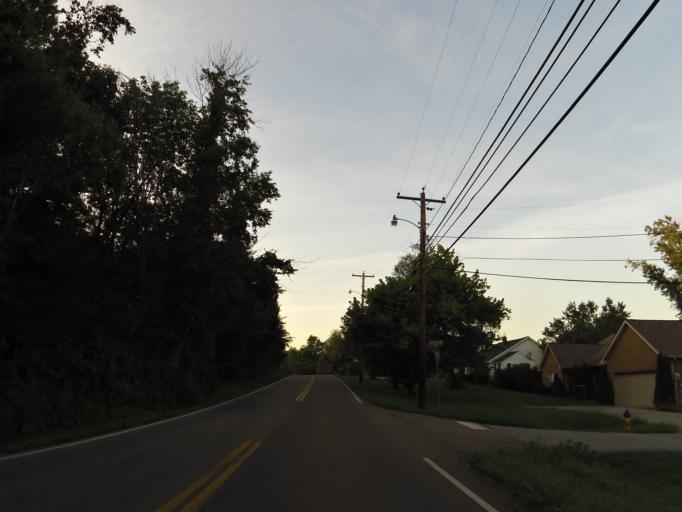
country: US
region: Tennessee
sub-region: Blount County
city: Maryville
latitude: 35.7181
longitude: -83.9645
